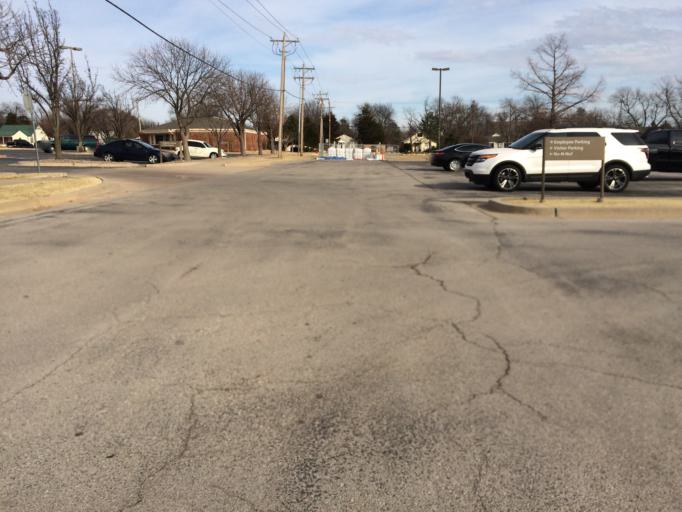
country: US
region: Oklahoma
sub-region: Cleveland County
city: Norman
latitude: 35.2287
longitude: -97.4389
